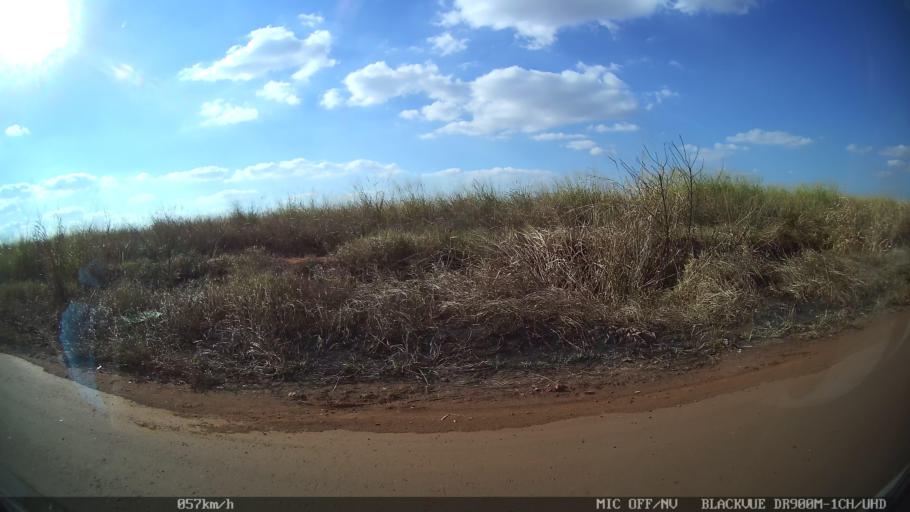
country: BR
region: Sao Paulo
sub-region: Americana
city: Americana
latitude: -22.7819
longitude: -47.3649
